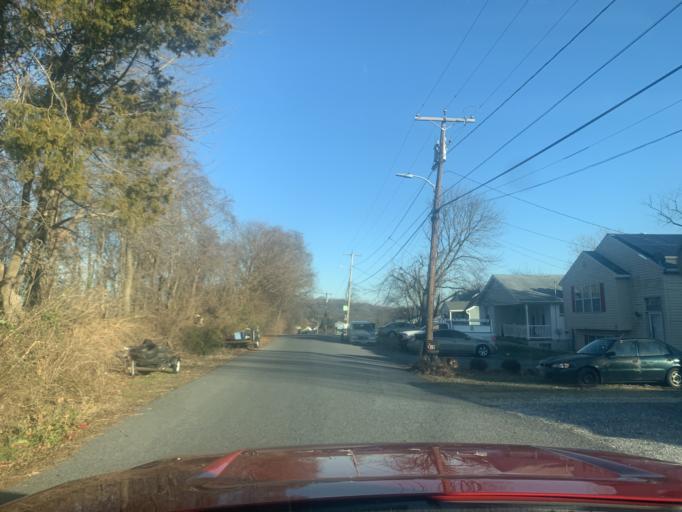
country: US
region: Maryland
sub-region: Anne Arundel County
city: Brooklyn Park
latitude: 39.2040
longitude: -76.6095
